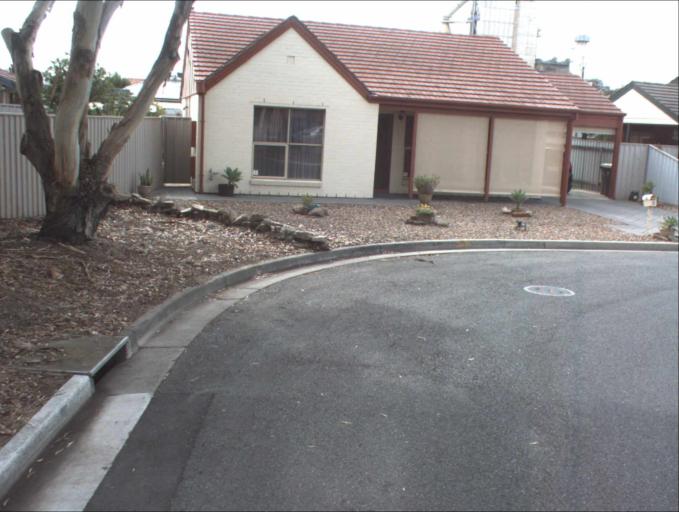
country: AU
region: South Australia
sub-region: Port Adelaide Enfield
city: Birkenhead
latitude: -34.8303
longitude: 138.4982
